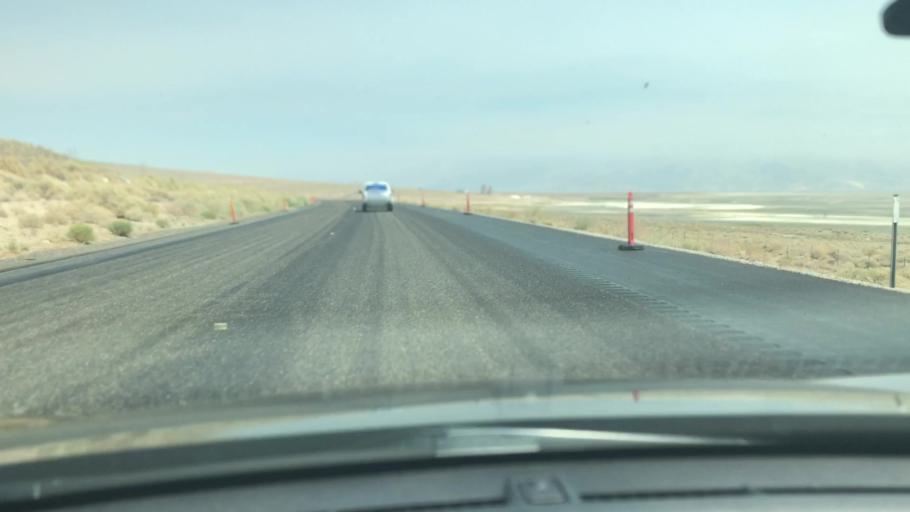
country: US
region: California
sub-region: Inyo County
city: Lone Pine
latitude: 36.4511
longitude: -118.0344
